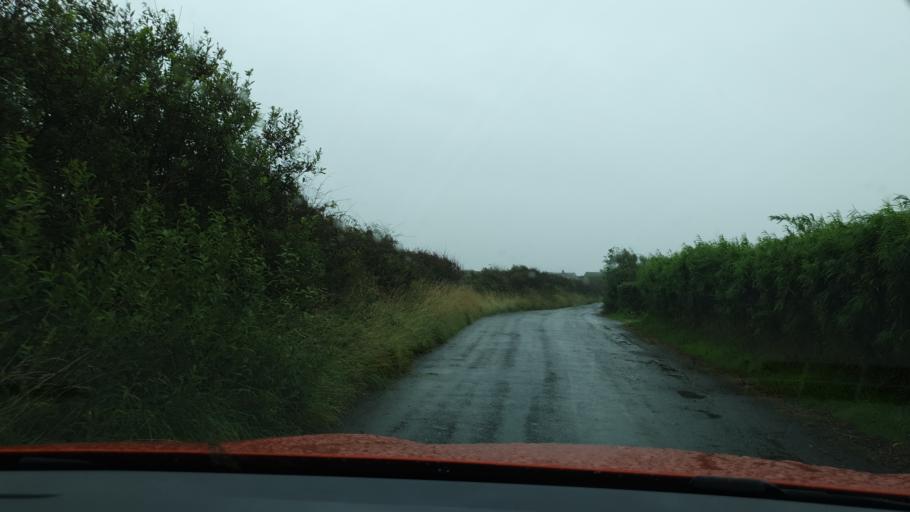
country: GB
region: England
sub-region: Cumbria
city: Barrow in Furness
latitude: 54.1223
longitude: -3.2594
